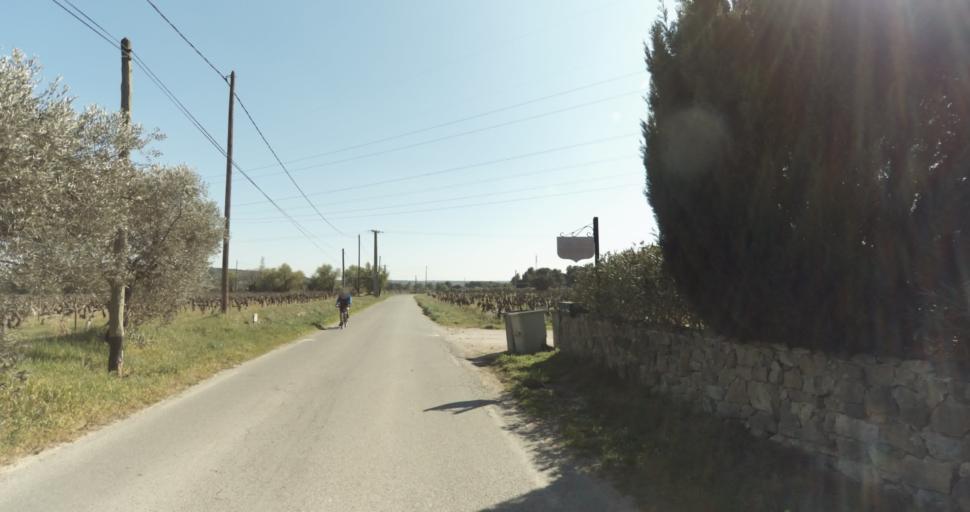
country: FR
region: Provence-Alpes-Cote d'Azur
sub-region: Departement des Bouches-du-Rhone
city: Pelissanne
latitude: 43.6468
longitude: 5.1818
